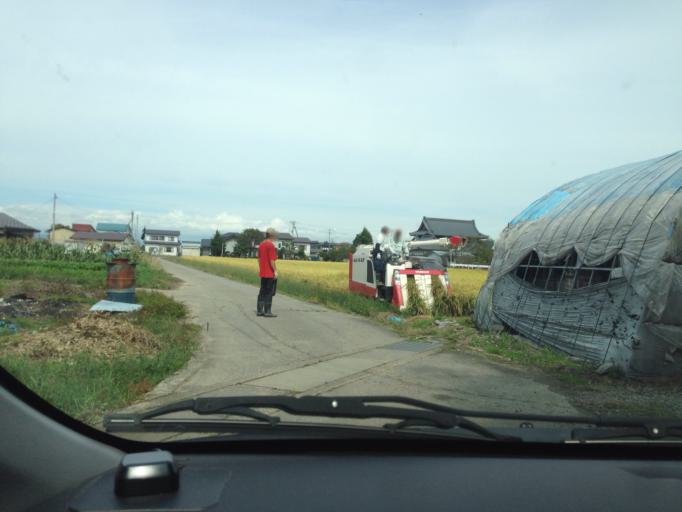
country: JP
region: Fukushima
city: Kitakata
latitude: 37.5031
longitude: 139.8475
